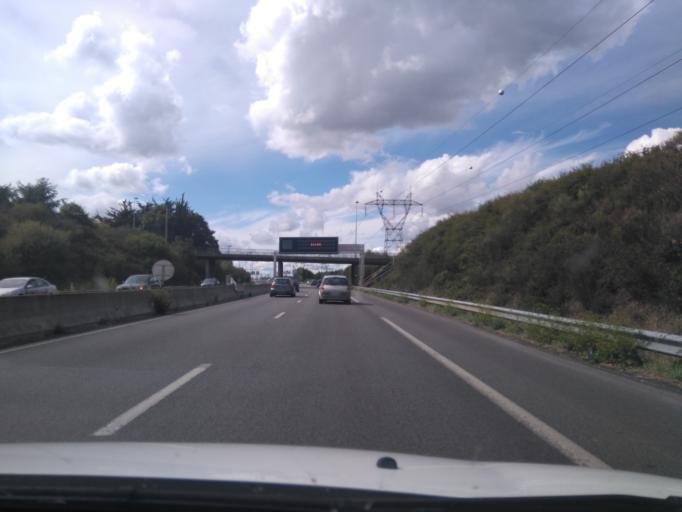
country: FR
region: Pays de la Loire
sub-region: Departement de la Loire-Atlantique
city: Bouguenais
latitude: 47.1775
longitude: -1.5999
